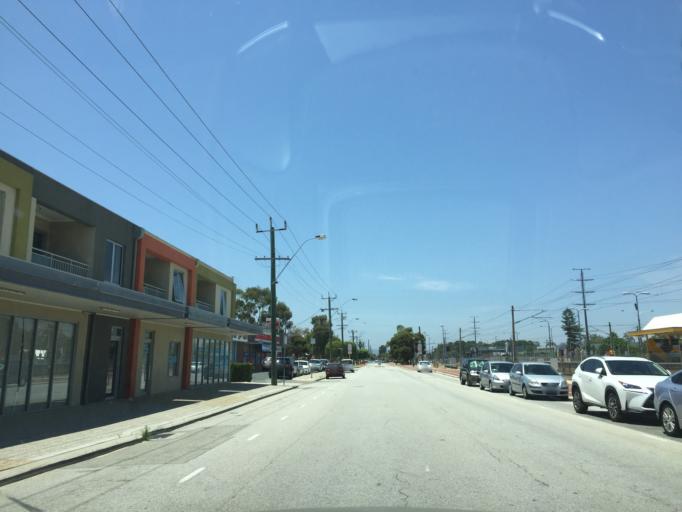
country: AU
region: Western Australia
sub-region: Canning
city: Queens Park
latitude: -32.0070
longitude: 115.9387
